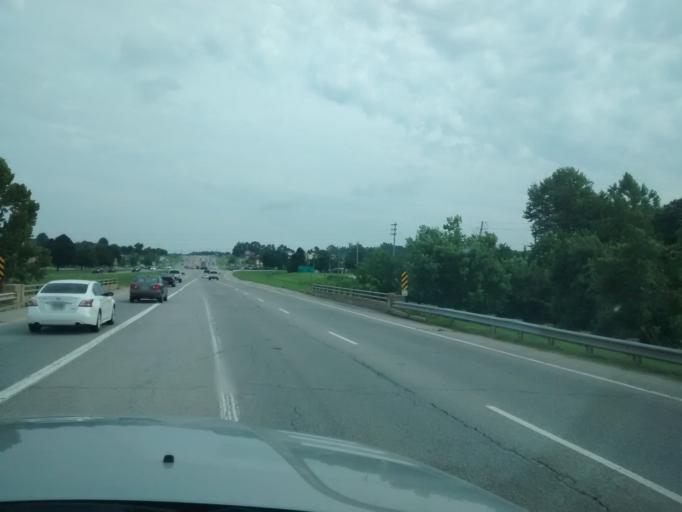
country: US
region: Arkansas
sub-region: Washington County
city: Johnson
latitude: 36.1190
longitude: -94.1449
